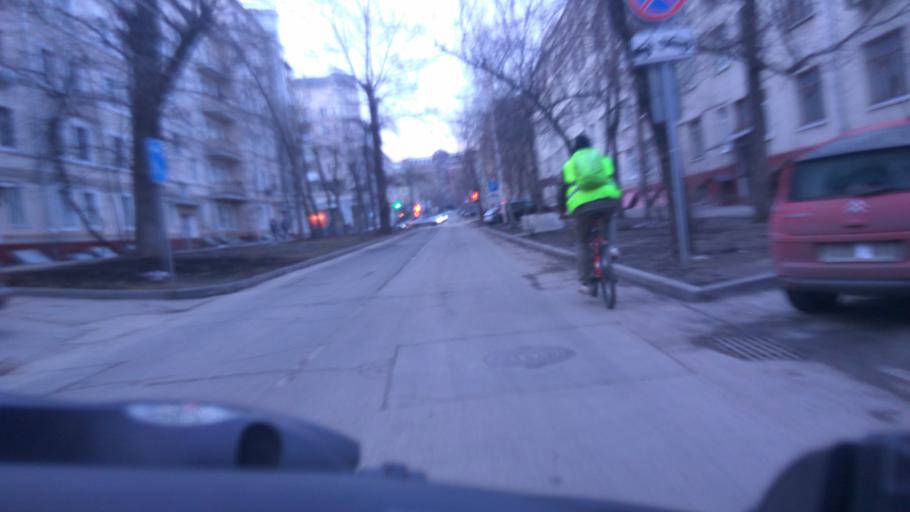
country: RU
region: Moskovskaya
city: Presnenskiy
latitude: 55.7576
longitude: 37.5533
